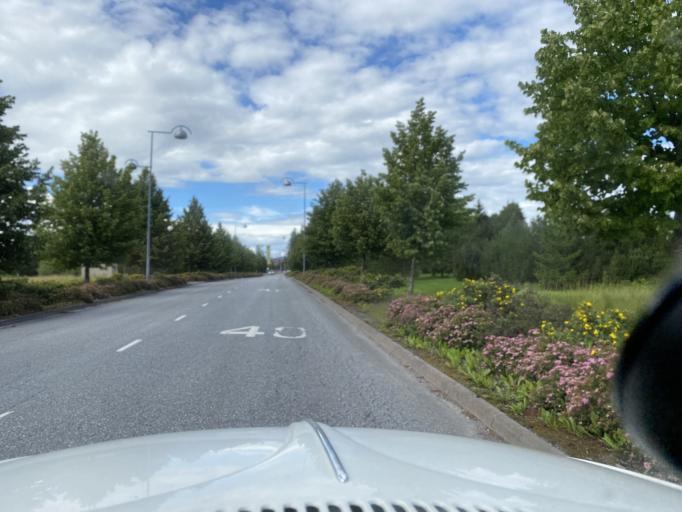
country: FI
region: Satakunta
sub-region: Pori
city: Huittinen
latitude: 61.1745
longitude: 22.7070
